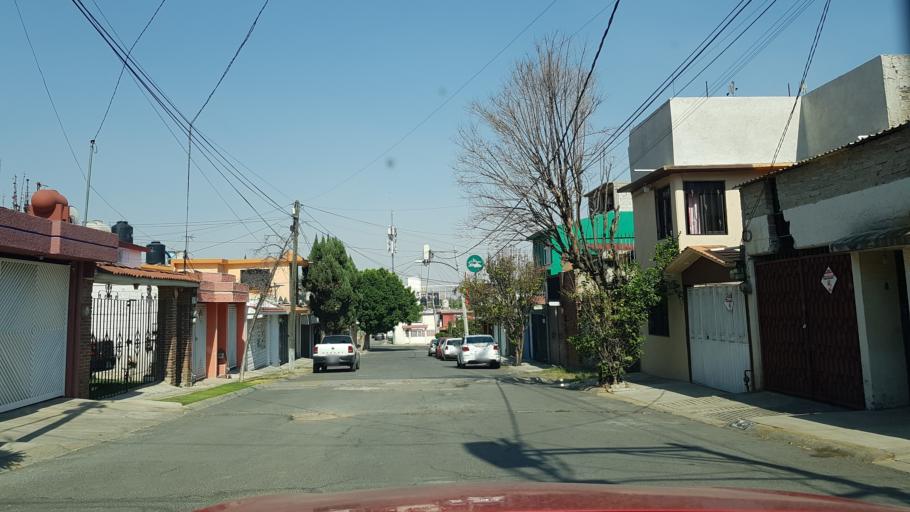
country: MX
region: Mexico
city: Cuautitlan Izcalli
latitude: 19.6478
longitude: -99.2102
